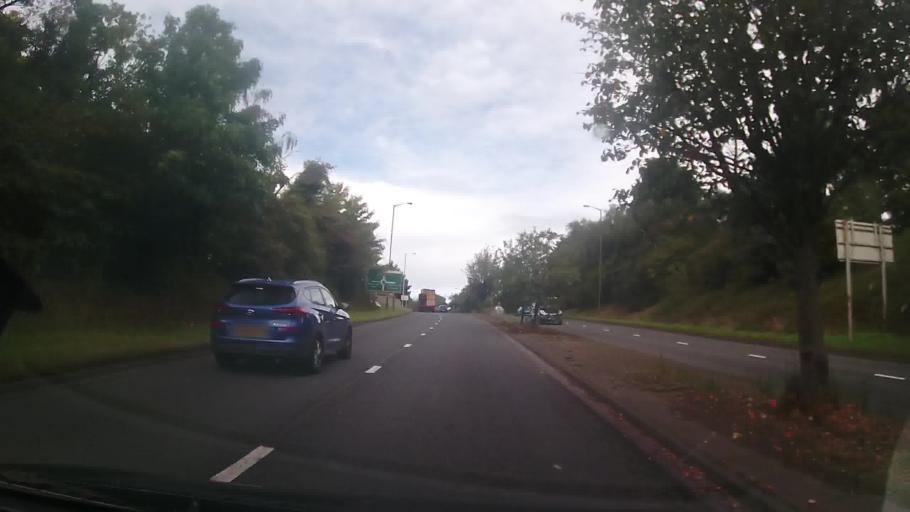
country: GB
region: England
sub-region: Worcestershire
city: Kidderminster
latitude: 52.3869
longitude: -2.2442
